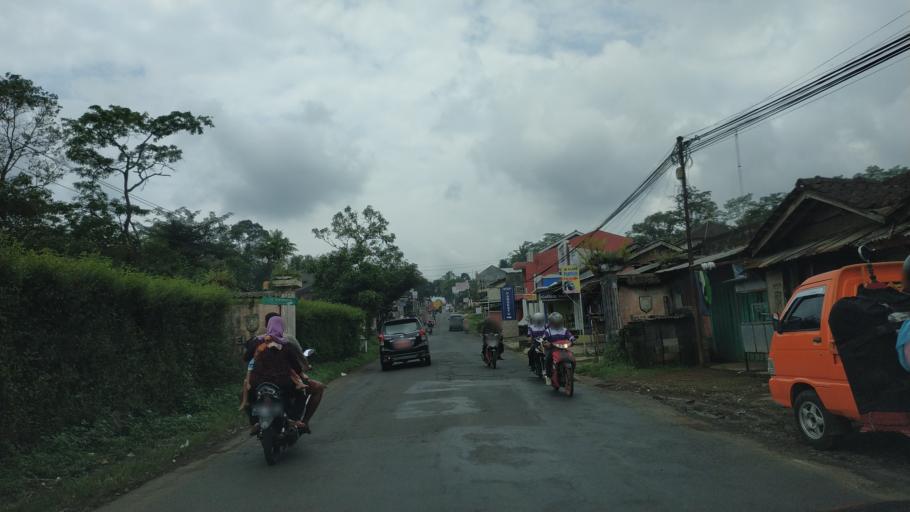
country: ID
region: Central Java
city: Weleri
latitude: -7.0949
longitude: 110.0570
